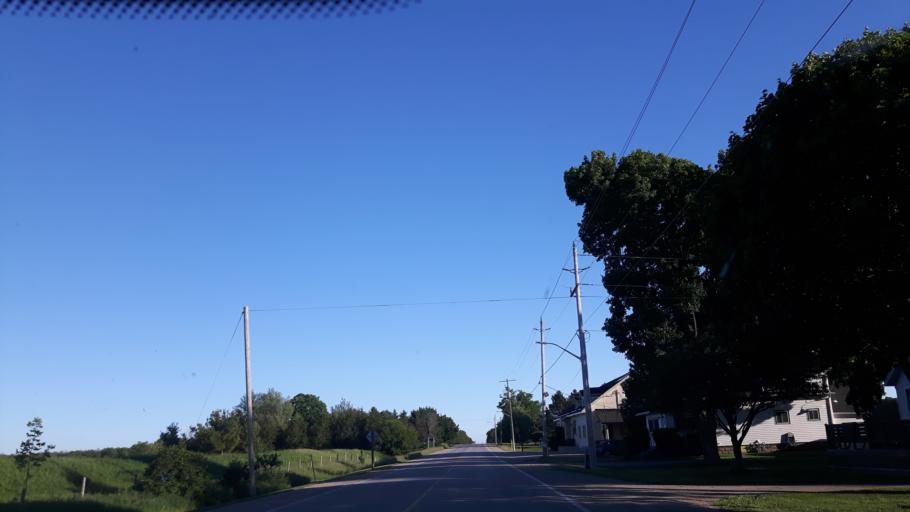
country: CA
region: Ontario
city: Goderich
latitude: 43.6431
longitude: -81.6025
